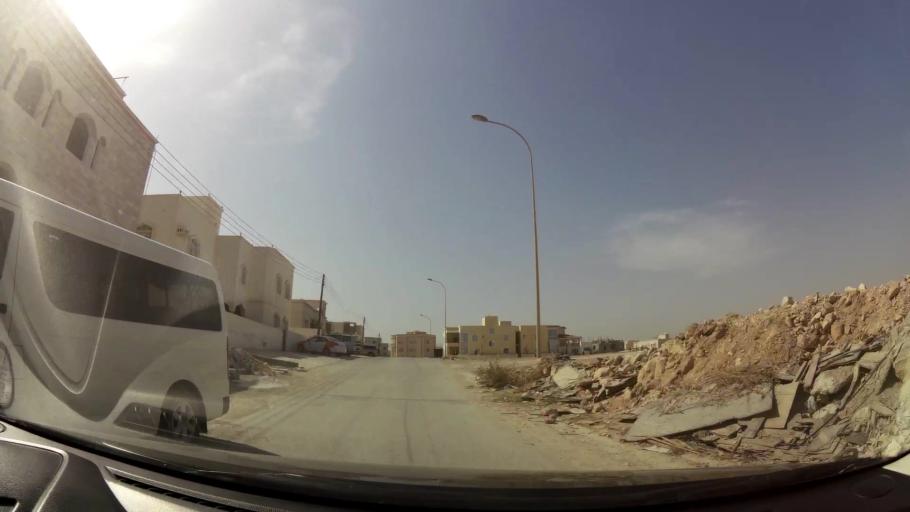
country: OM
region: Zufar
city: Salalah
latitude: 16.9994
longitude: 54.0193
